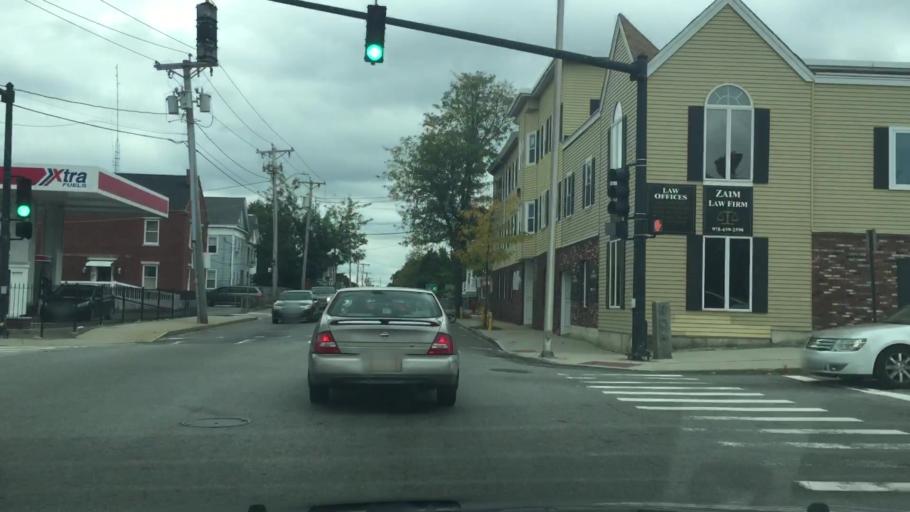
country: US
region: Massachusetts
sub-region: Middlesex County
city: Lowell
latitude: 42.6372
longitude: -71.3090
